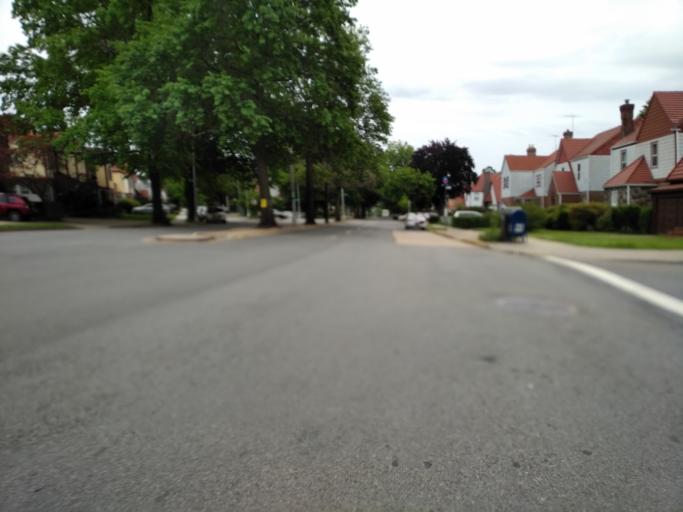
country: US
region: New York
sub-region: Nassau County
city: East Atlantic Beach
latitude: 40.7505
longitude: -73.7923
